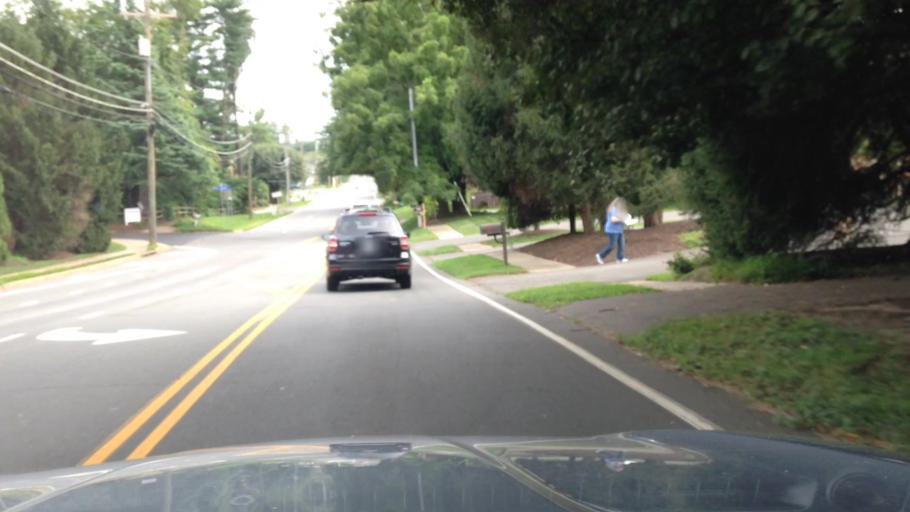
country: US
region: Virginia
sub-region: Fairfax County
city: Pimmit Hills
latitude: 38.9284
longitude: -77.1974
